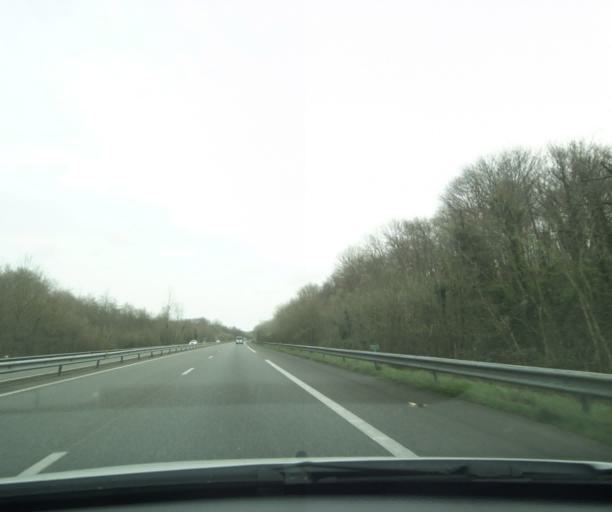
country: FR
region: Aquitaine
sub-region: Departement des Landes
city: Peyrehorade
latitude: 43.5247
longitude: -1.1417
